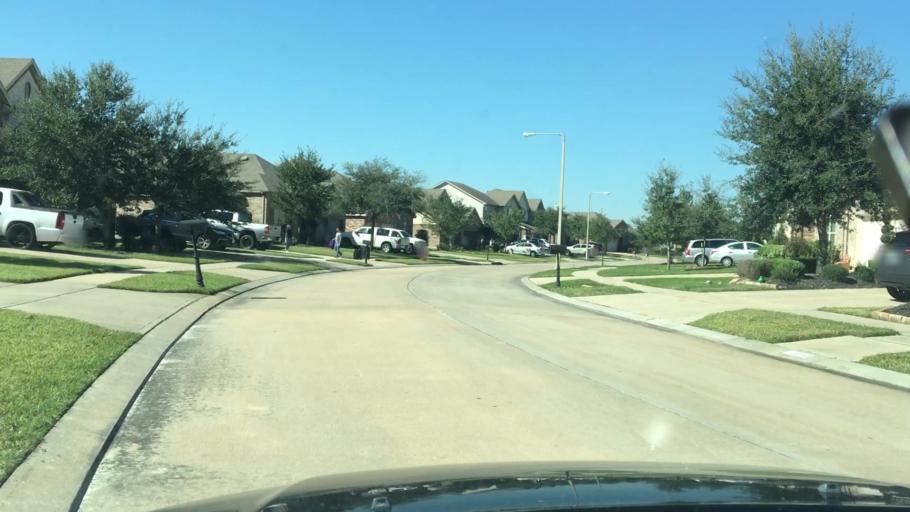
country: US
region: Texas
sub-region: Galveston County
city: Friendswood
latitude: 29.4738
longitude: -95.1652
